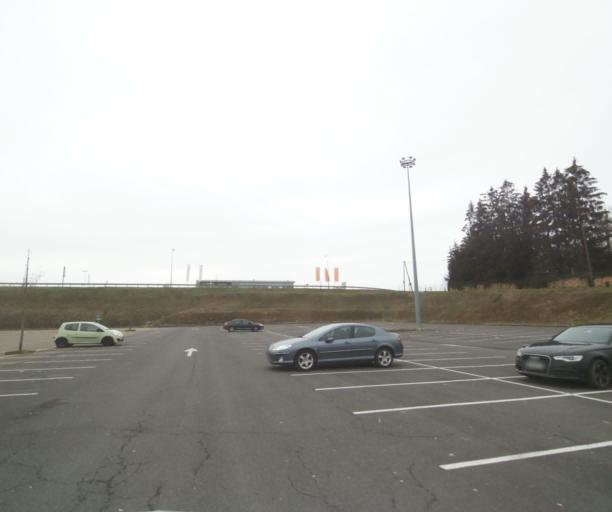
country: FR
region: Champagne-Ardenne
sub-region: Departement de la Haute-Marne
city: Saint-Dizier
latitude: 48.6279
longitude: 4.9696
